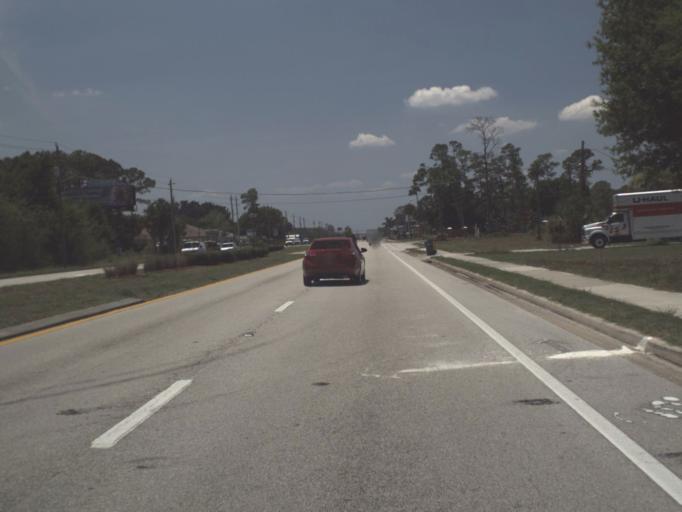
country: US
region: Florida
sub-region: Brevard County
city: June Park
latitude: 28.0790
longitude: -80.6877
